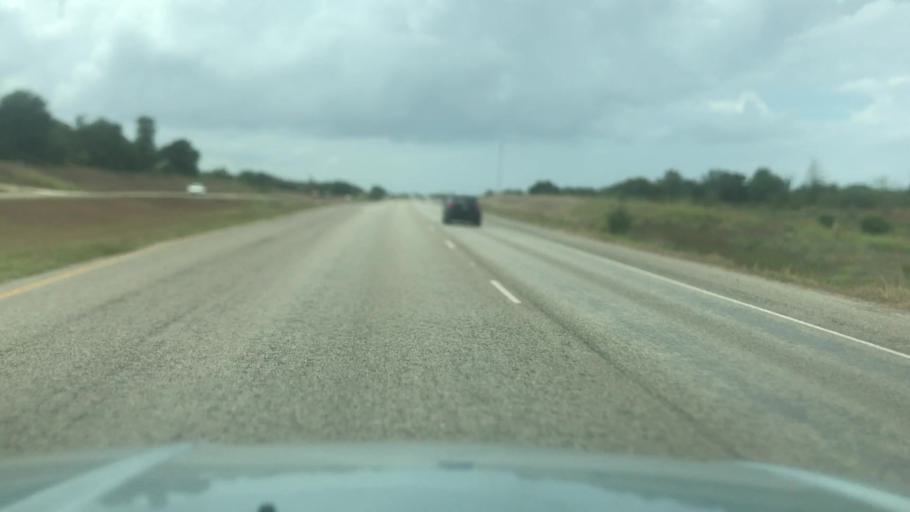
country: US
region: Texas
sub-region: Colorado County
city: Weimar
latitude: 29.8063
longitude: -96.6732
